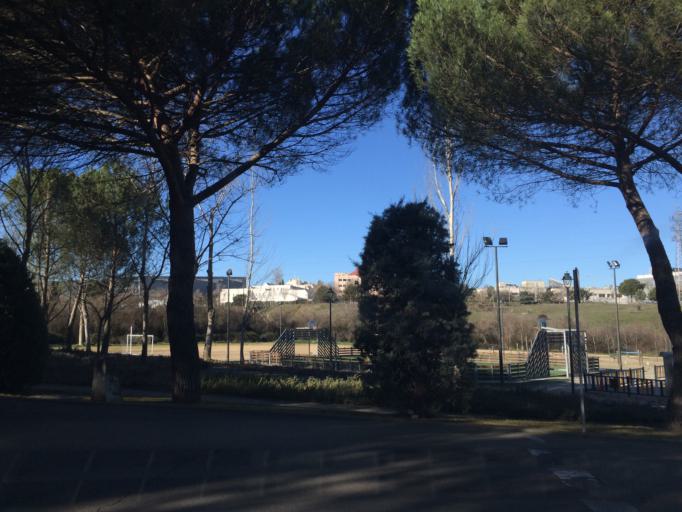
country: ES
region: Madrid
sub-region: Provincia de Madrid
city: Tres Cantos
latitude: 40.6117
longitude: -3.6914
